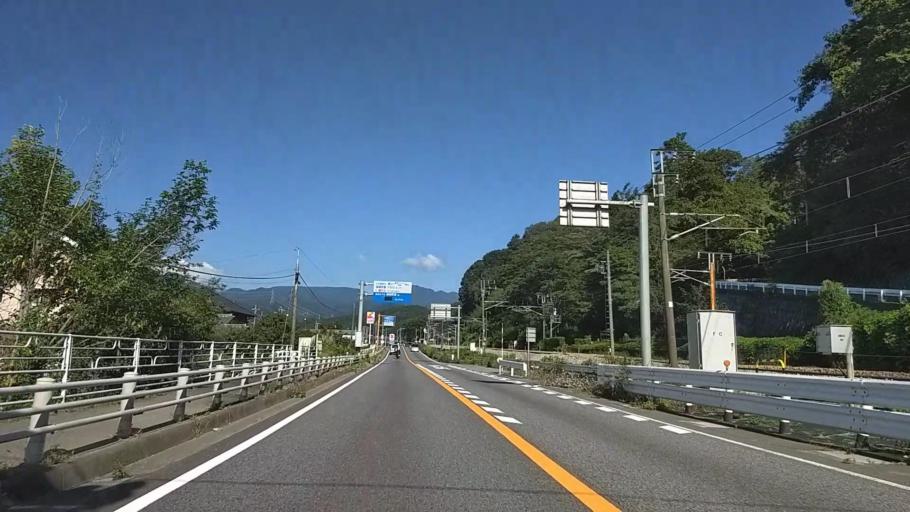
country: JP
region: Gunma
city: Annaka
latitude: 36.3277
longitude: 138.7562
